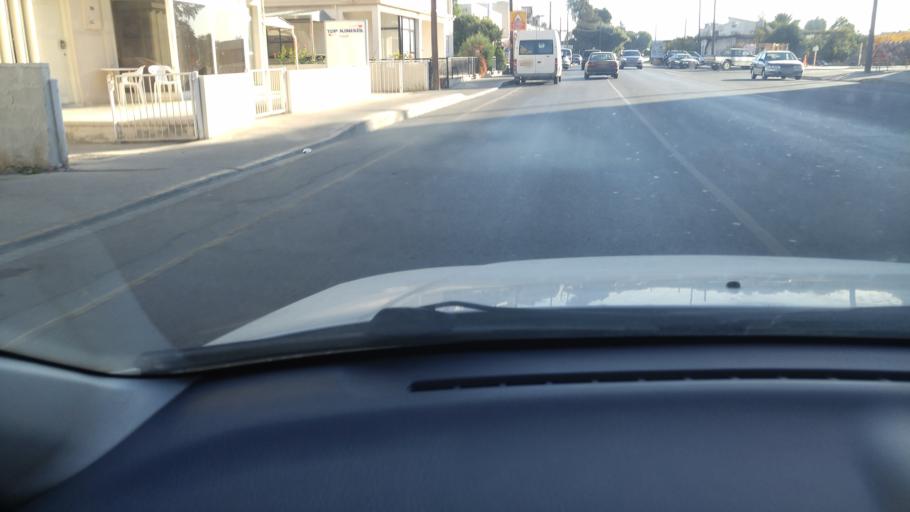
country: CY
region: Limassol
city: Limassol
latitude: 34.6598
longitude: 33.0050
